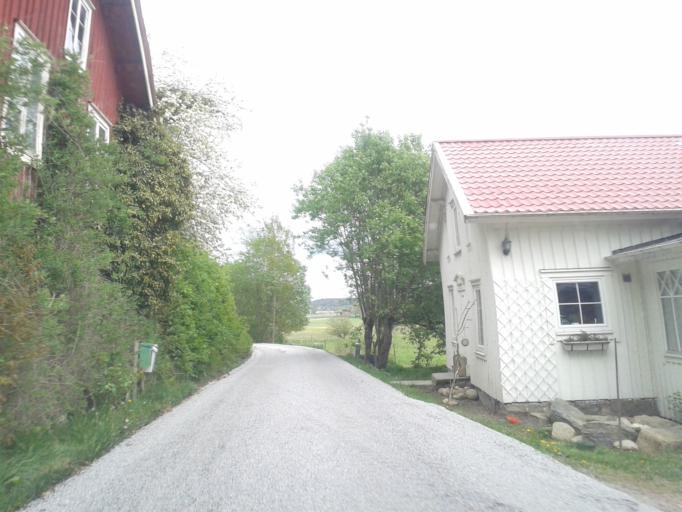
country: SE
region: Vaestra Goetaland
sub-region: Kungalvs Kommun
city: Kode
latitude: 57.8936
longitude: 11.9058
